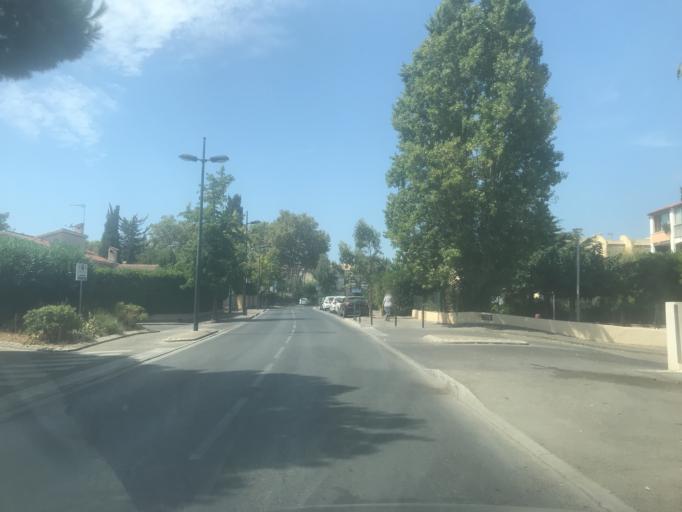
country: FR
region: Provence-Alpes-Cote d'Azur
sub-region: Departement du Var
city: Six-Fours-les-Plages
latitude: 43.0911
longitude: 5.8469
